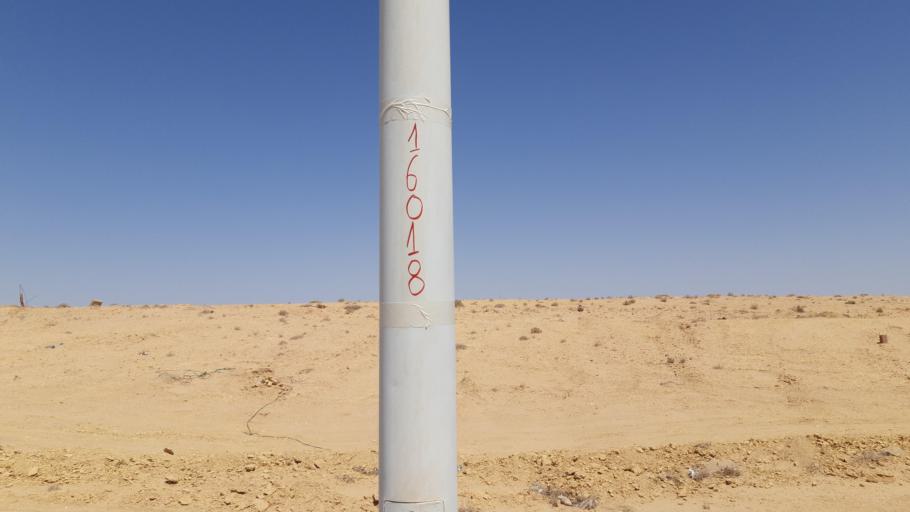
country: TN
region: Tawzar
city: Degache
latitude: 33.9896
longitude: 8.2054
